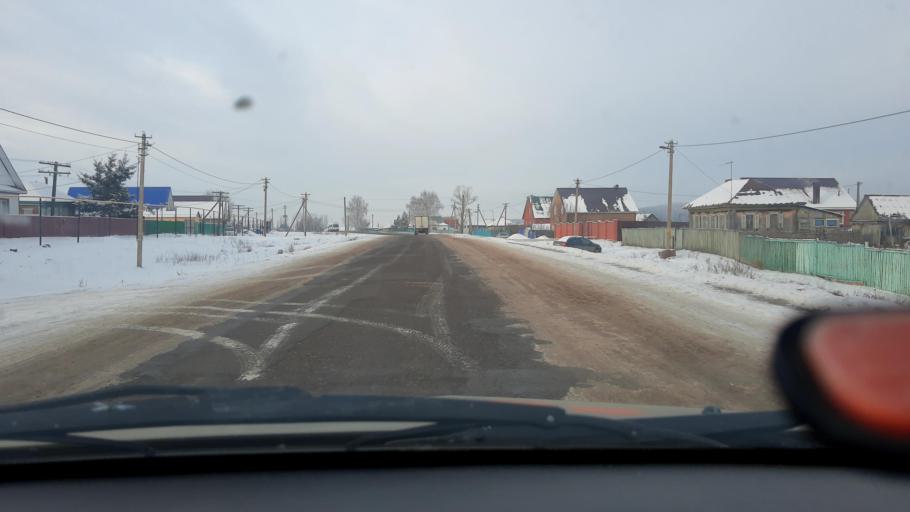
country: RU
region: Bashkortostan
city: Avdon
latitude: 54.3588
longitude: 55.8432
